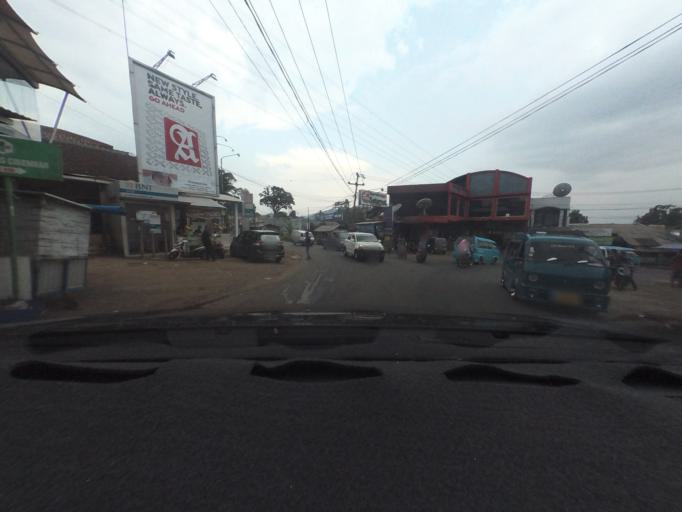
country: ID
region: West Java
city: Gunungkalong
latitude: -6.9535
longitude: 106.7680
